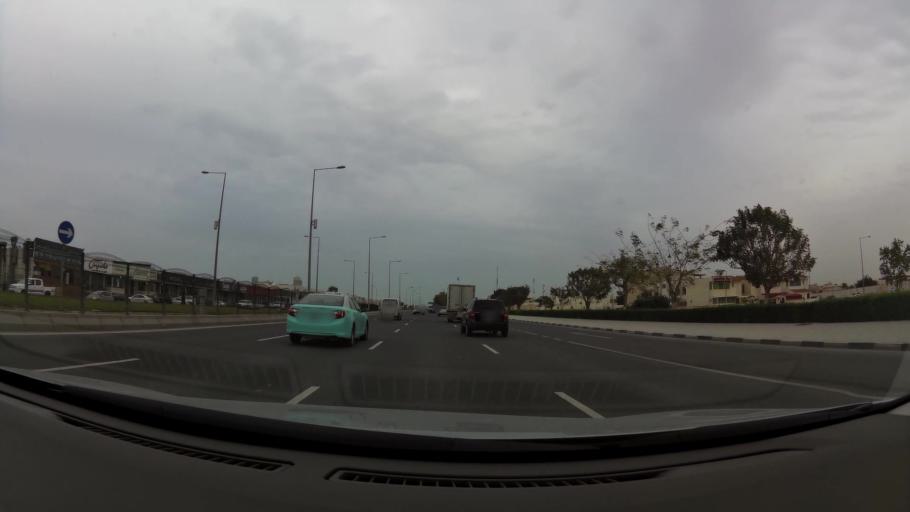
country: QA
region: Baladiyat ad Dawhah
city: Doha
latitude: 25.3202
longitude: 51.4903
